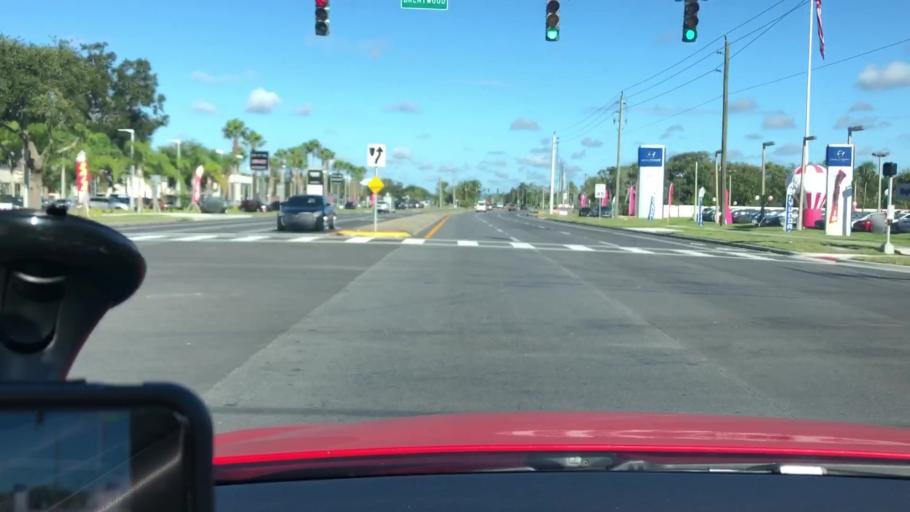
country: US
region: Florida
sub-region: Volusia County
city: Holly Hill
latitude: 29.2224
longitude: -81.0486
